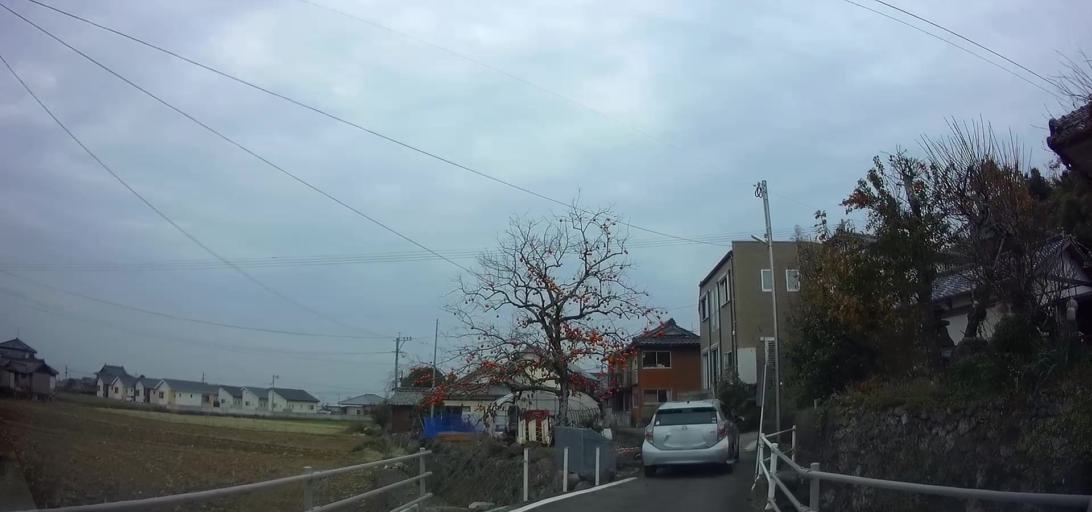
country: JP
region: Nagasaki
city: Shimabara
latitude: 32.6652
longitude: 130.2984
